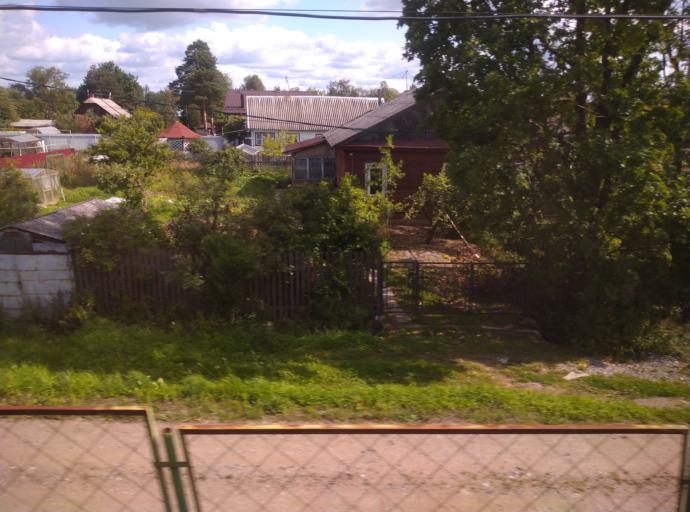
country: RU
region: Leningrad
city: Ul'yanovka
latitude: 59.6405
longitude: 30.7507
